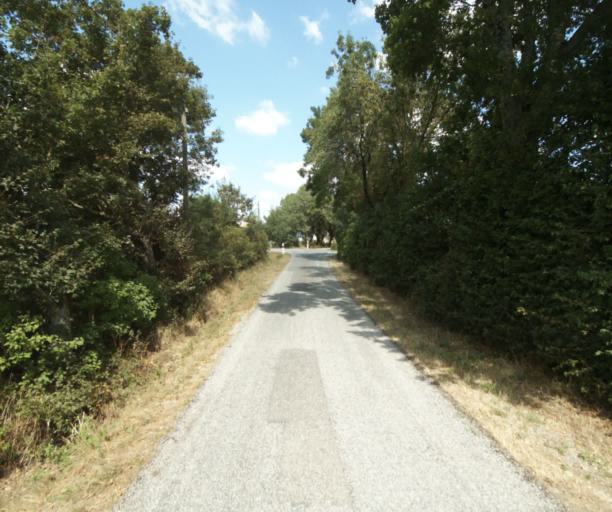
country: FR
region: Midi-Pyrenees
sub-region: Departement de la Haute-Garonne
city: Auriac-sur-Vendinelle
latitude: 43.4781
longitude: 1.8181
